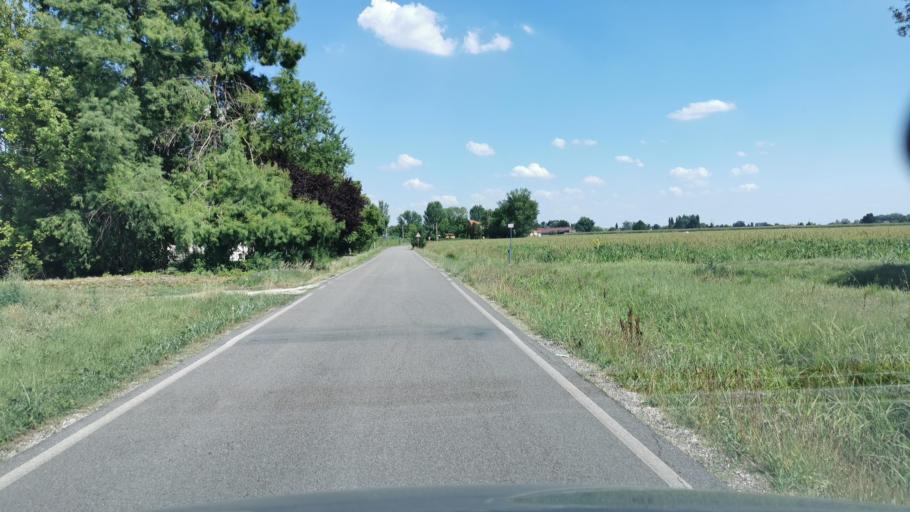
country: IT
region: Emilia-Romagna
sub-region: Provincia di Modena
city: Fossoli
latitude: 44.8145
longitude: 10.8966
